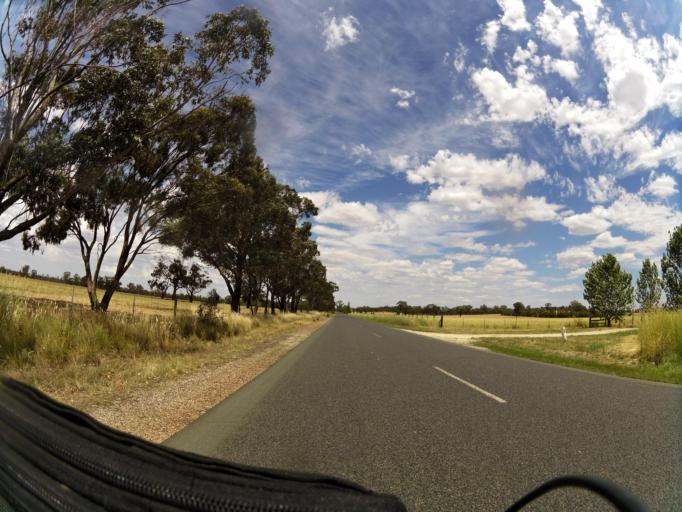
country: AU
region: Victoria
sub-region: Campaspe
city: Kyabram
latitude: -36.7752
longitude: 145.1111
